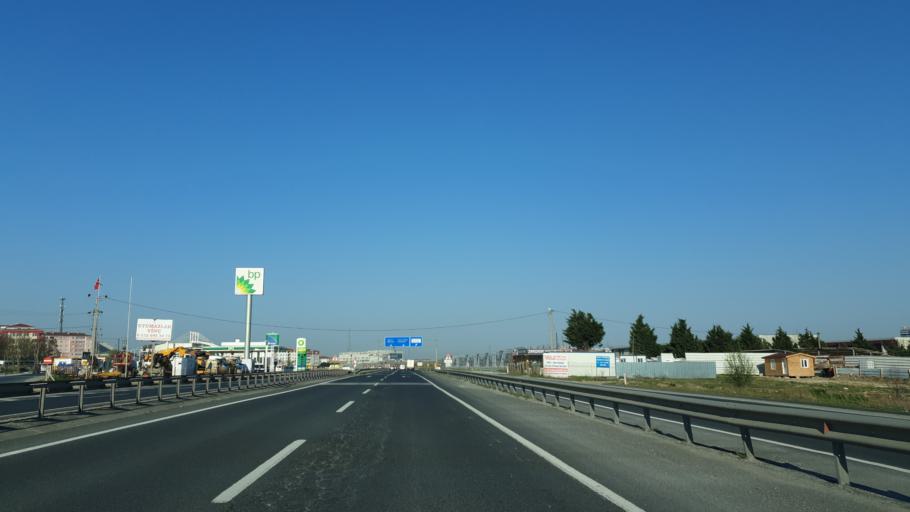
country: TR
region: Tekirdag
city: Cerkezkoey
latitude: 41.2649
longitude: 27.9457
